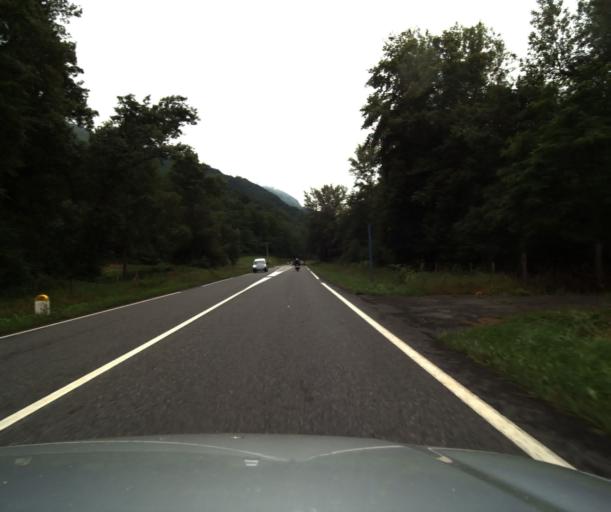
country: FR
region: Midi-Pyrenees
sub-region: Departement des Hautes-Pyrenees
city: Pierrefitte-Nestalas
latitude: 42.9717
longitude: -0.0639
